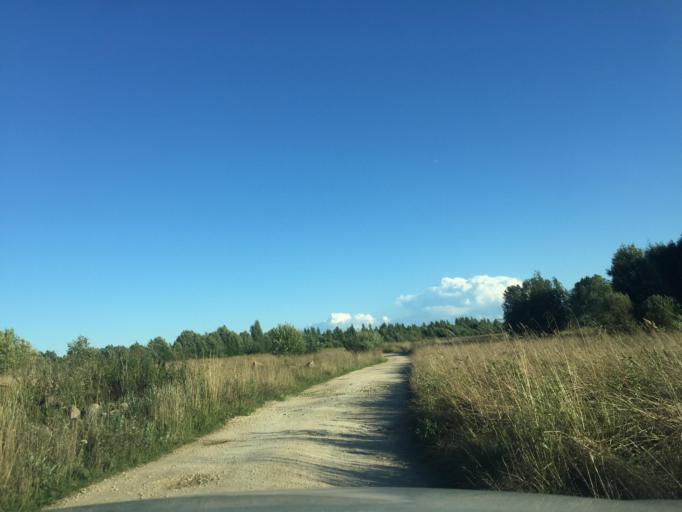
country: RU
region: Leningrad
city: Rozhdestveno
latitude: 59.3306
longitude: 29.9974
